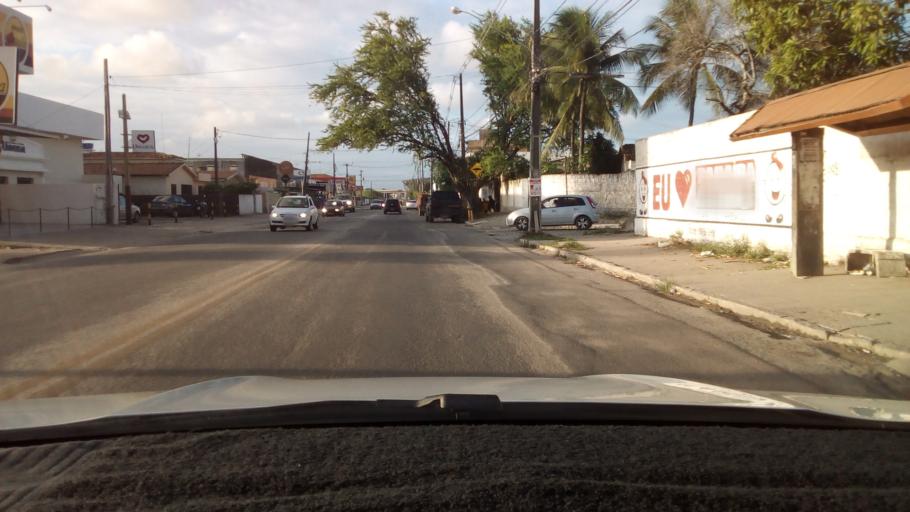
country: BR
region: Paraiba
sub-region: Joao Pessoa
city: Joao Pessoa
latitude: -7.1753
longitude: -34.8739
